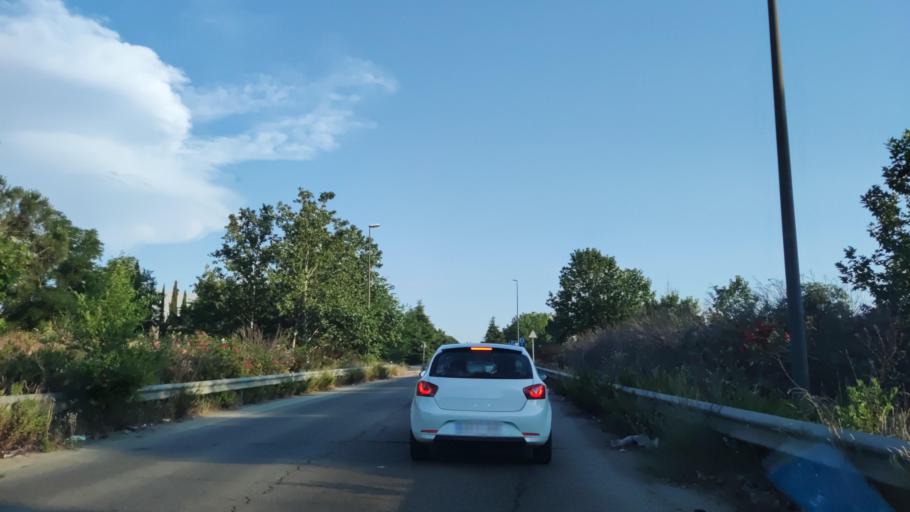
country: ES
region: Madrid
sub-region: Provincia de Madrid
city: Pinto
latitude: 40.2690
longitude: -3.6946
